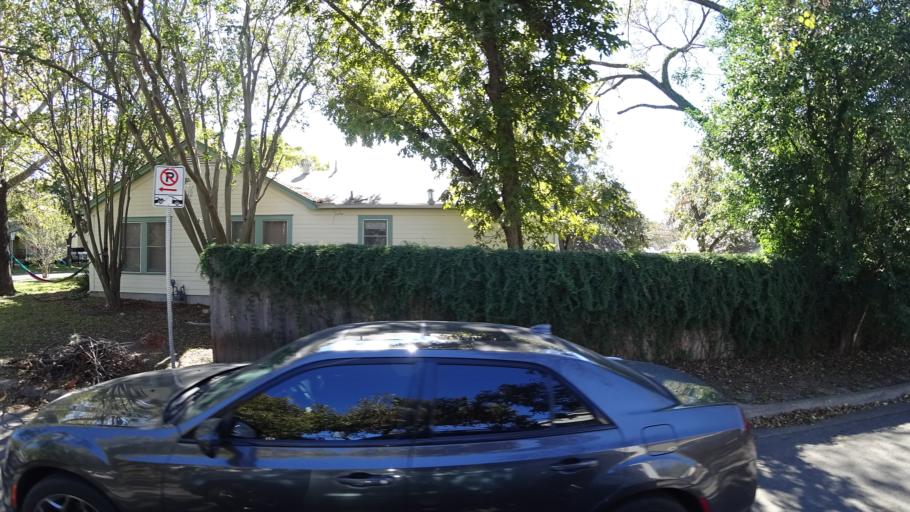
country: US
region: Texas
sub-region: Travis County
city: Austin
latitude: 30.3172
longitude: -97.7419
